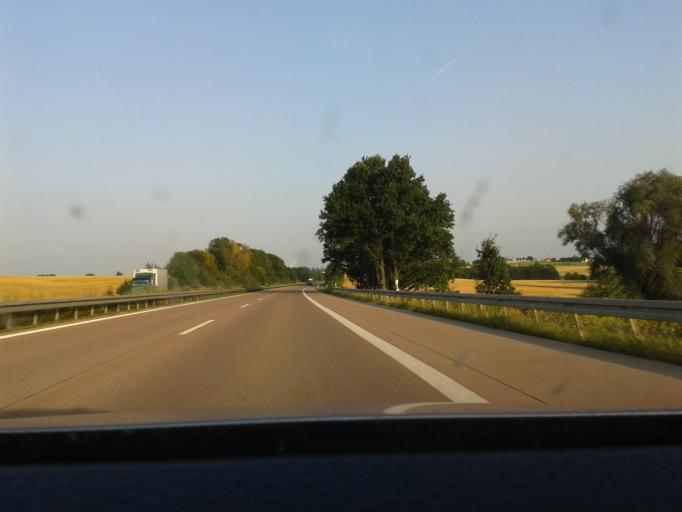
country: DE
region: Saxony
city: Bockelwitz
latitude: 51.2161
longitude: 12.9402
